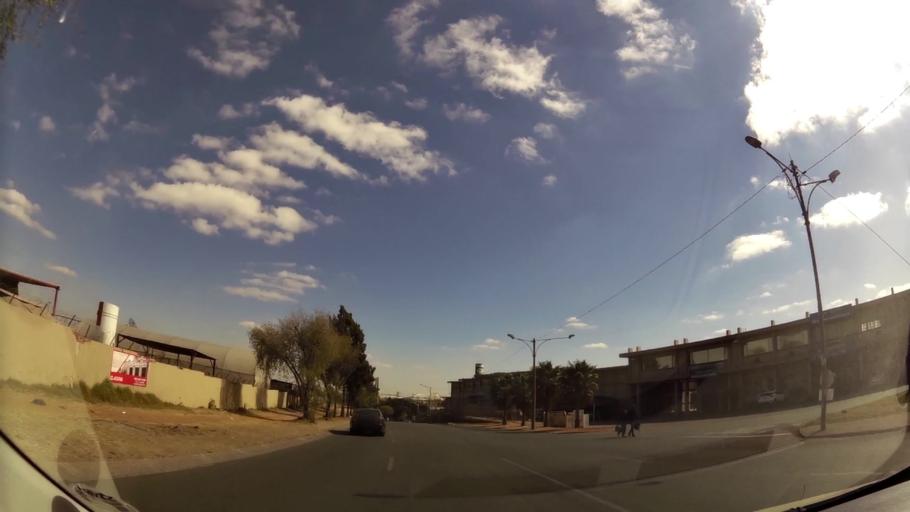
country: ZA
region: Gauteng
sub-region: West Rand District Municipality
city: Krugersdorp
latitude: -26.1186
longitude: 27.8093
